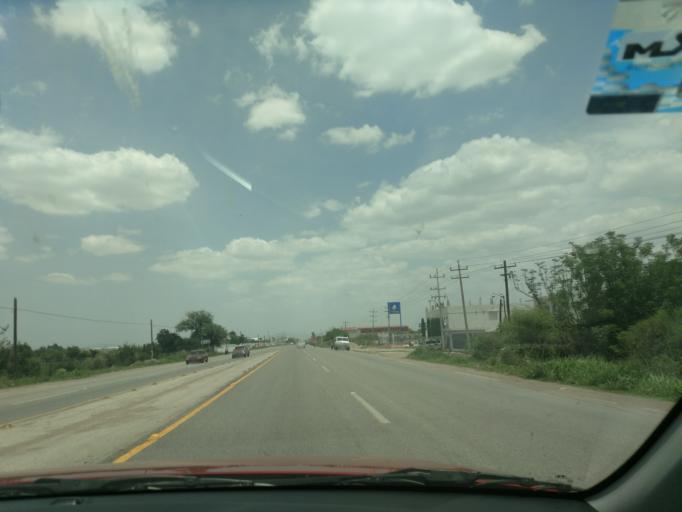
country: MX
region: San Luis Potosi
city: Ciudad Fernandez
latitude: 21.9415
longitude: -100.0410
